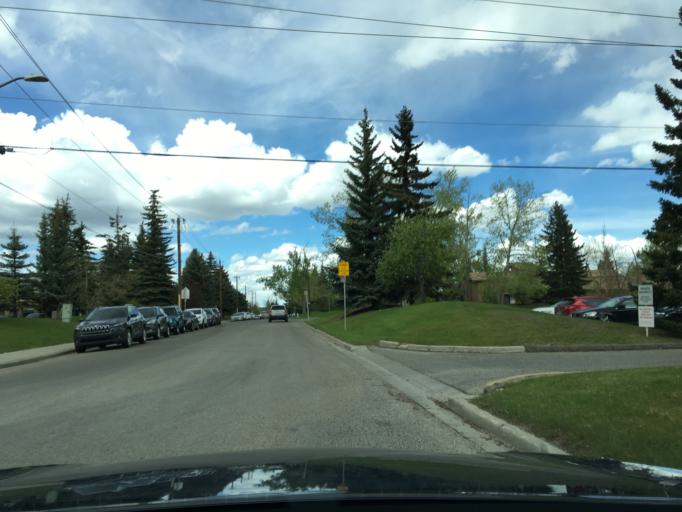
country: CA
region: Alberta
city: Calgary
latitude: 50.9093
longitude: -114.0630
